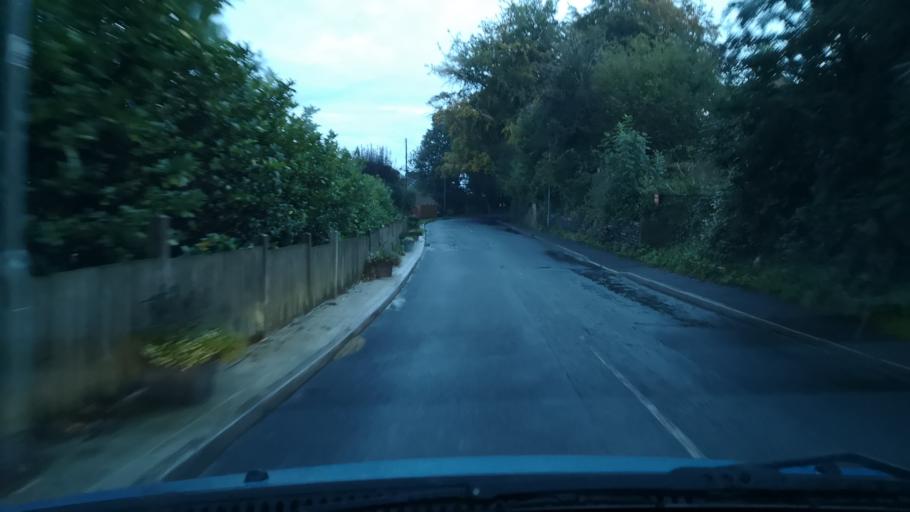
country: GB
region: England
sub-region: Kirklees
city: Batley
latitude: 53.7280
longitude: -1.6366
